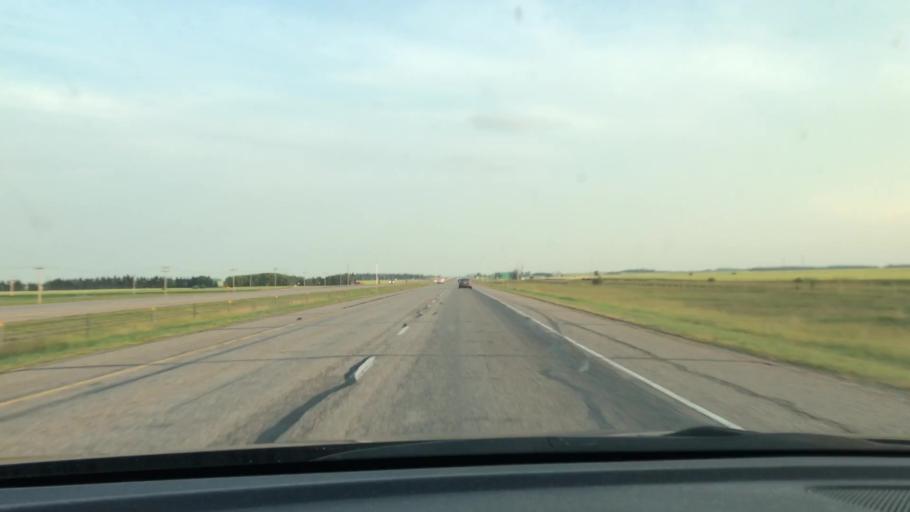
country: CA
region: Alberta
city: Olds
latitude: 51.8570
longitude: -114.0256
